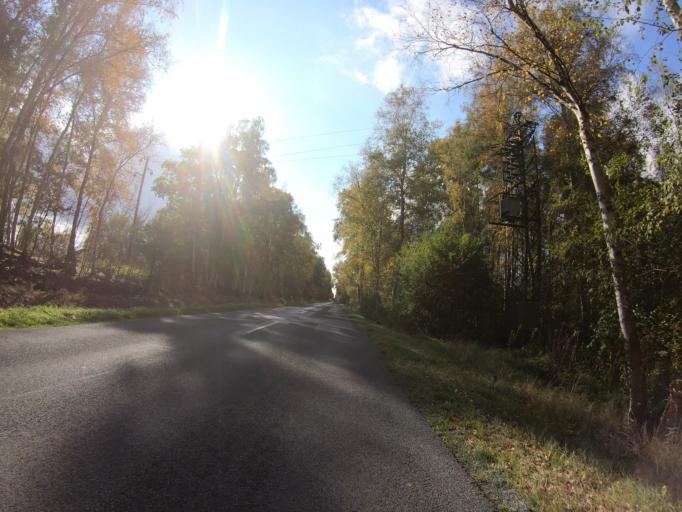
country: DE
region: Lower Saxony
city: Sassenburg
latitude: 52.5618
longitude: 10.6256
